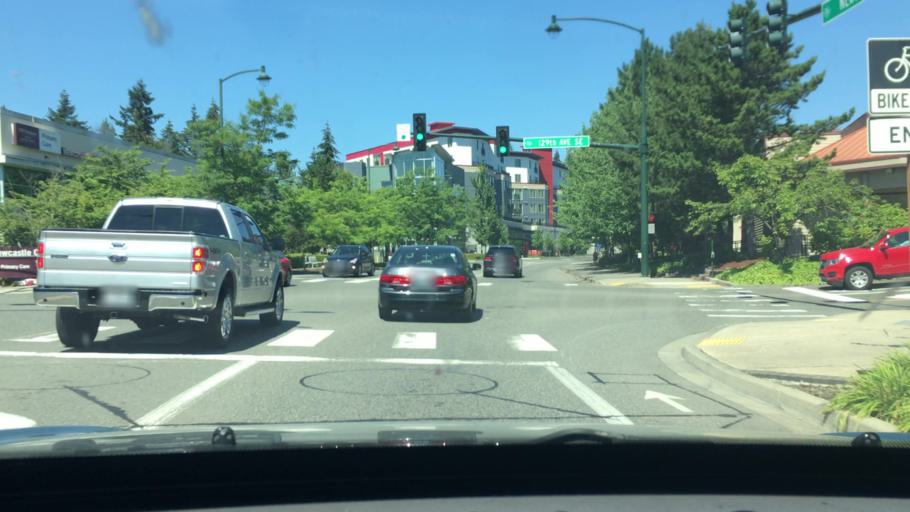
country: US
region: Washington
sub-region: King County
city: Newcastle
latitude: 47.5380
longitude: -122.1673
